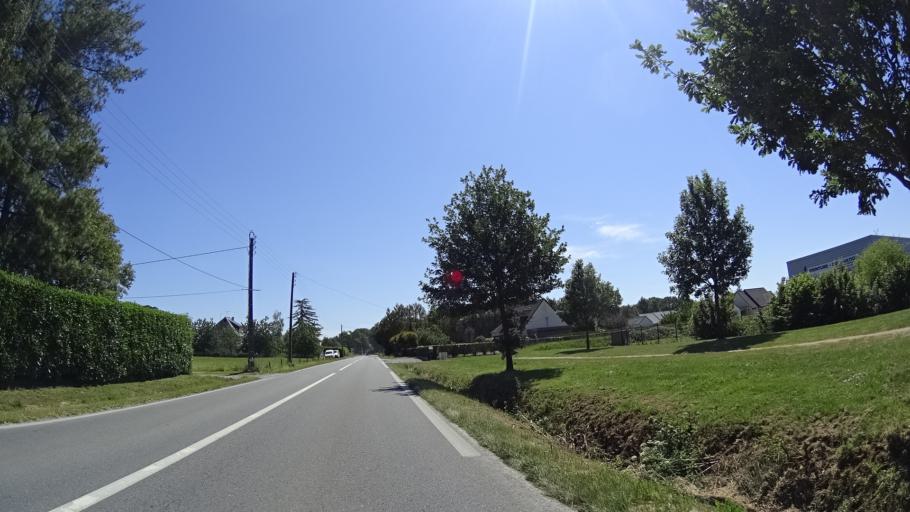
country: FR
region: Brittany
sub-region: Departement d'Ille-et-Vilaine
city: Messac
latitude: 47.8251
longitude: -1.7880
